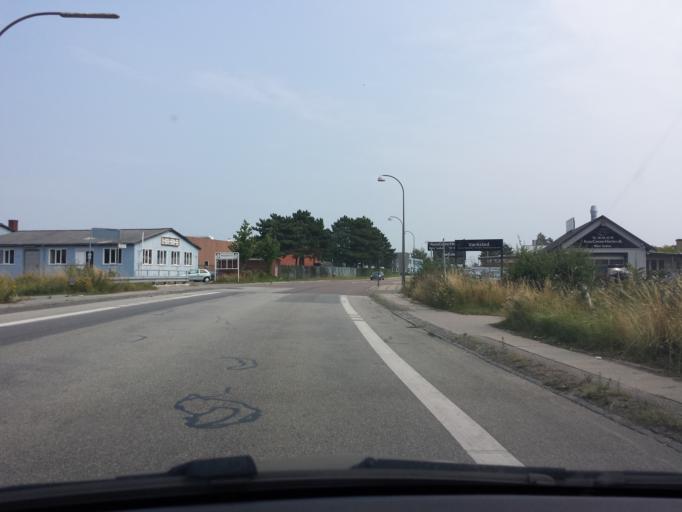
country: DK
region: Capital Region
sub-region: Herlev Kommune
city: Herlev
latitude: 55.7165
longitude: 12.4256
